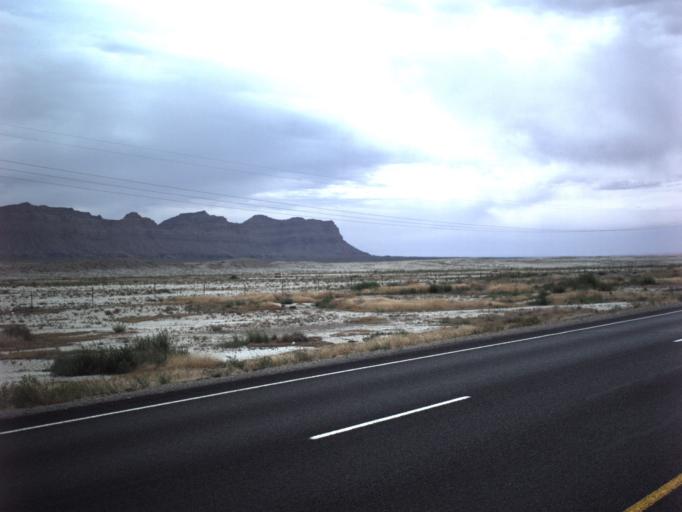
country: US
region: Utah
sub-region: Carbon County
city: East Carbon City
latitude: 39.1607
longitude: -110.3382
